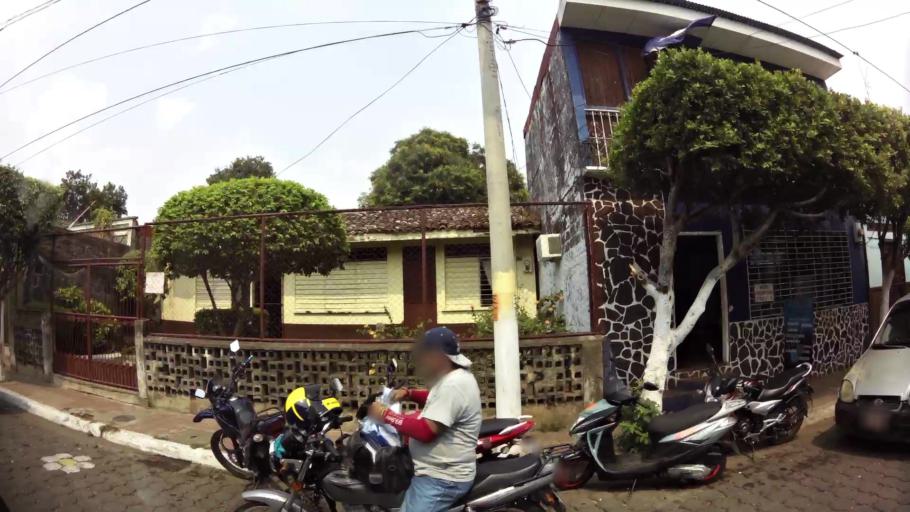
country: NI
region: Chinandega
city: Chinandega
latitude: 12.6273
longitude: -87.1300
